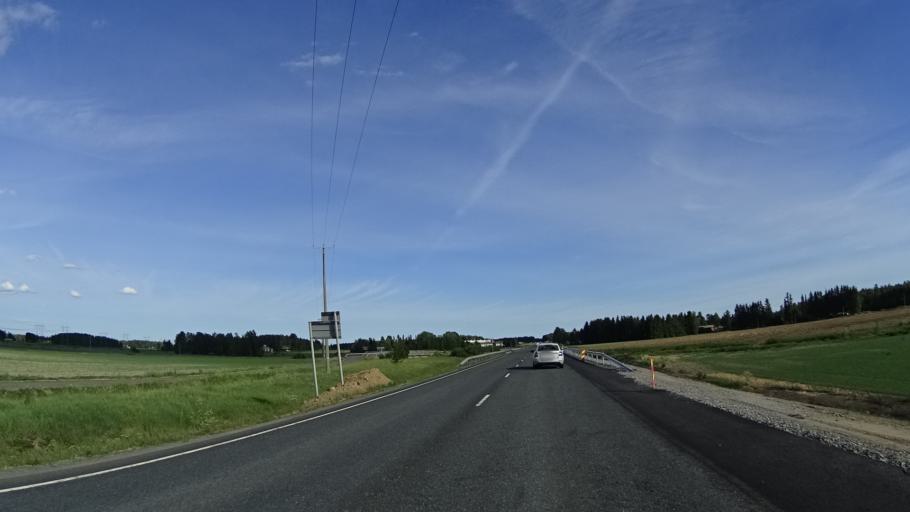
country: FI
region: Haeme
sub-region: Forssa
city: Forssa
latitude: 60.7662
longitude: 23.6863
